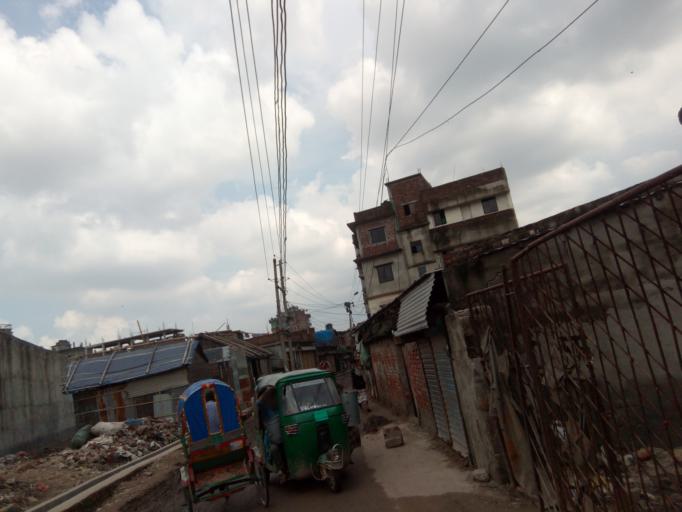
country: BD
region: Dhaka
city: Azimpur
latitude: 23.7331
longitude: 90.3642
